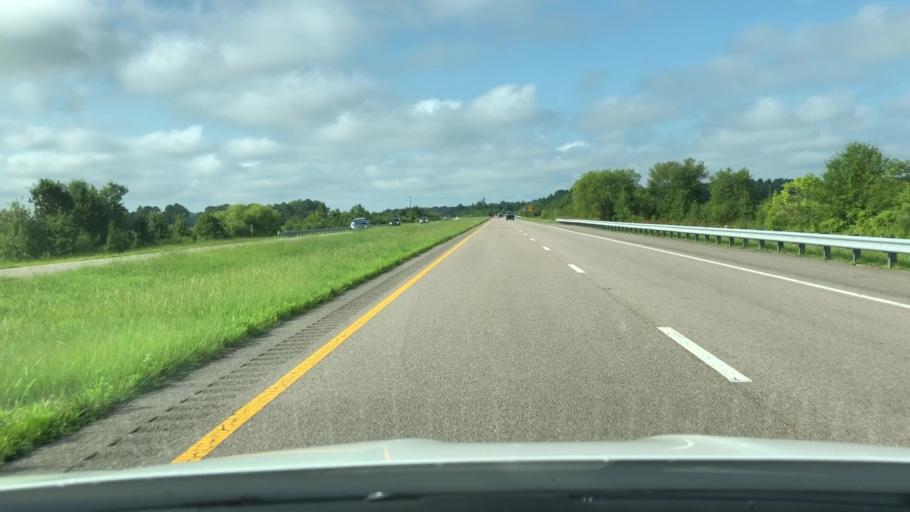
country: US
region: Virginia
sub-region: City of Portsmouth
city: Portsmouth Heights
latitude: 36.6944
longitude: -76.3458
